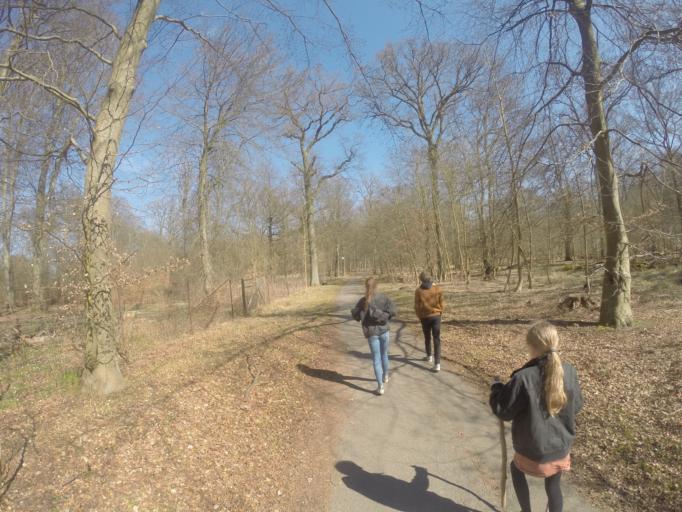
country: DK
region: Capital Region
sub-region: Rudersdal Kommune
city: Trorod
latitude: 55.8013
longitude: 12.5490
